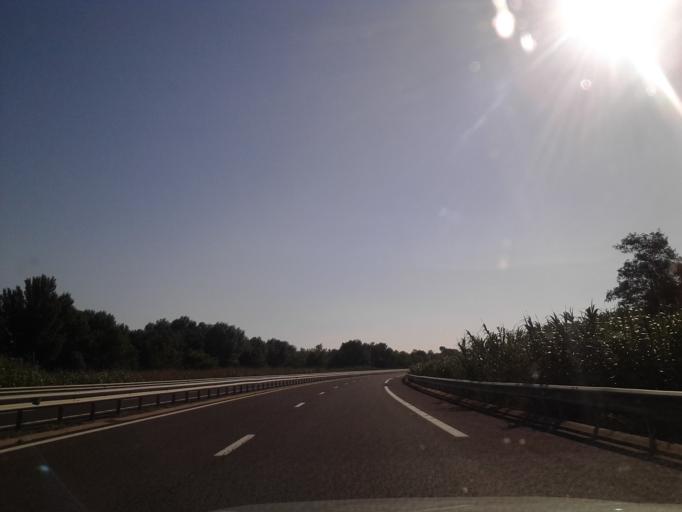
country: FR
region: Languedoc-Roussillon
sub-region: Departement des Pyrenees-Orientales
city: Ille-sur-Tet
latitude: 42.6930
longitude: 2.6438
